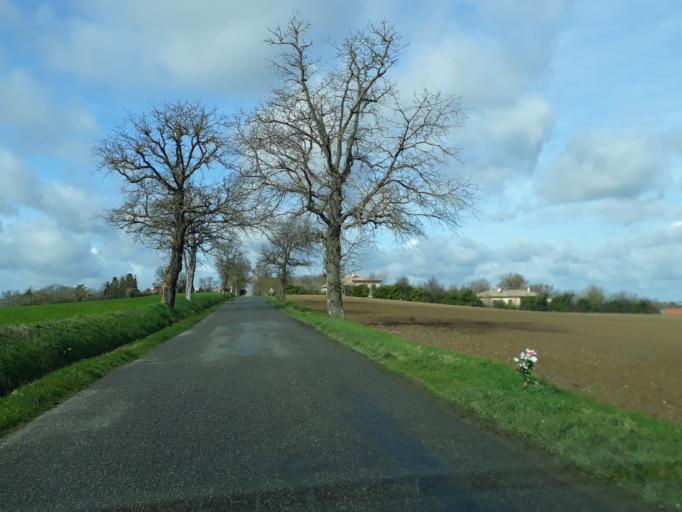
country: FR
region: Midi-Pyrenees
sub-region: Departement du Gers
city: Gimont
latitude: 43.6378
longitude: 1.0042
